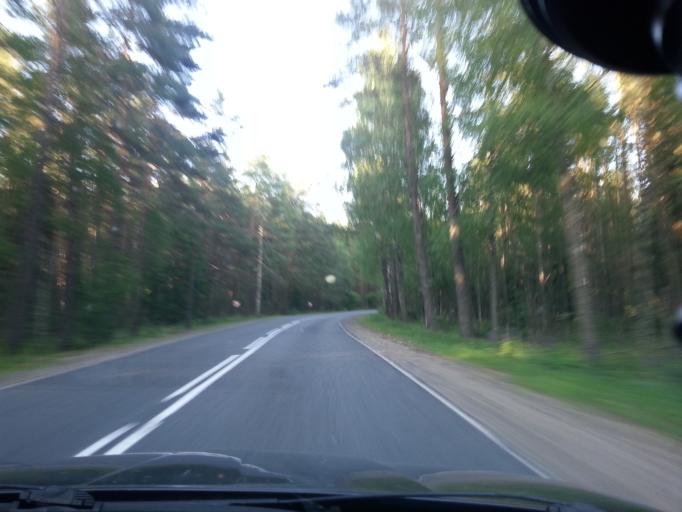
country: BY
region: Minsk
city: Narach
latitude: 54.9567
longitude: 26.6103
